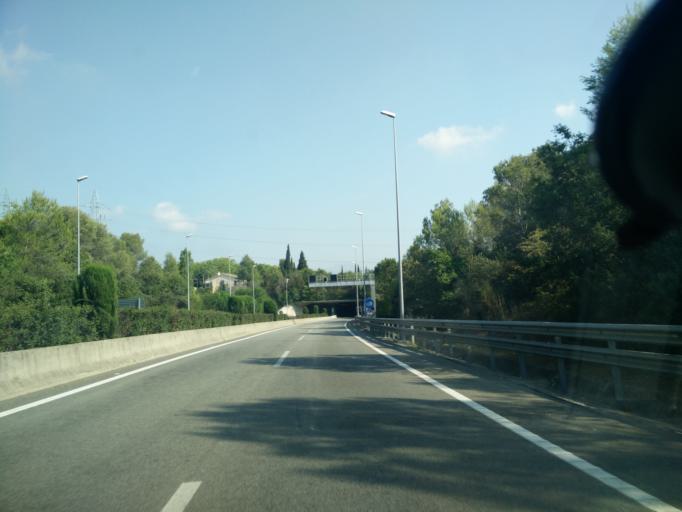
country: ES
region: Catalonia
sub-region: Provincia de Barcelona
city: Sant Cugat del Valles
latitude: 41.4559
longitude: 2.0673
